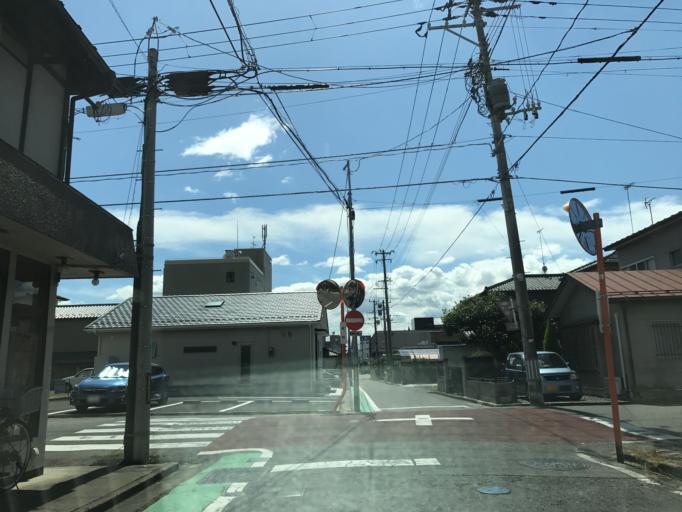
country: JP
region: Fukushima
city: Koriyama
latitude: 37.3876
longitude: 140.3778
